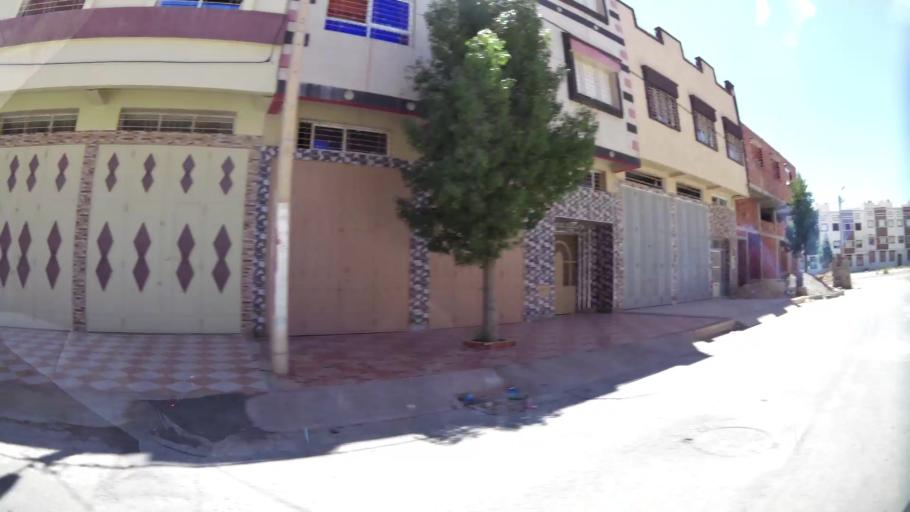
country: MA
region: Oriental
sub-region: Oujda-Angad
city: Oujda
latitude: 34.6570
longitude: -1.9446
